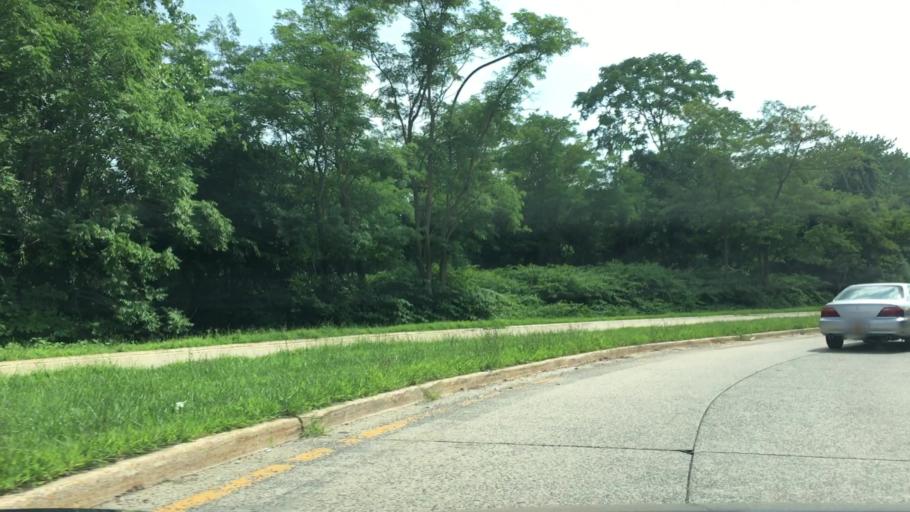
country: US
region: New York
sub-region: Nassau County
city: Merrick
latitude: 40.6645
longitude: -73.5671
